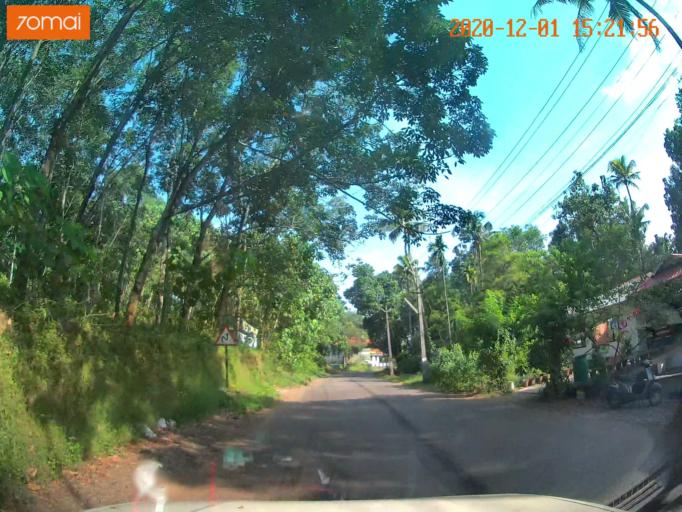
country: IN
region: Kerala
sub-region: Ernakulam
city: Muvattupuzha
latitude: 9.9466
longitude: 76.5455
